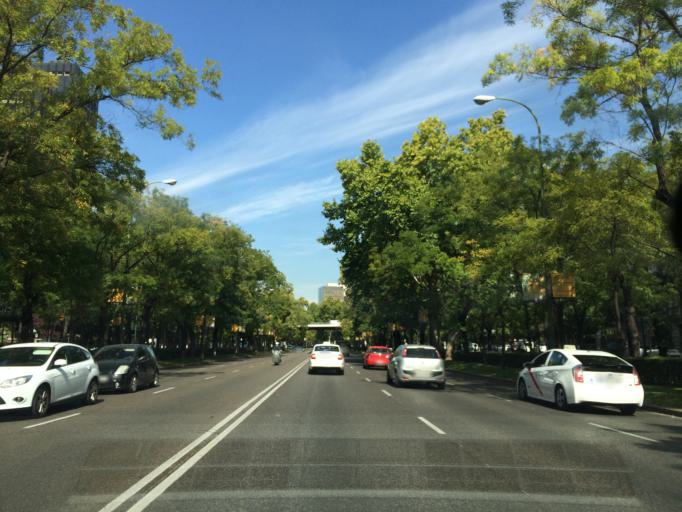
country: ES
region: Madrid
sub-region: Provincia de Madrid
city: Salamanca
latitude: 40.4310
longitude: -3.6889
